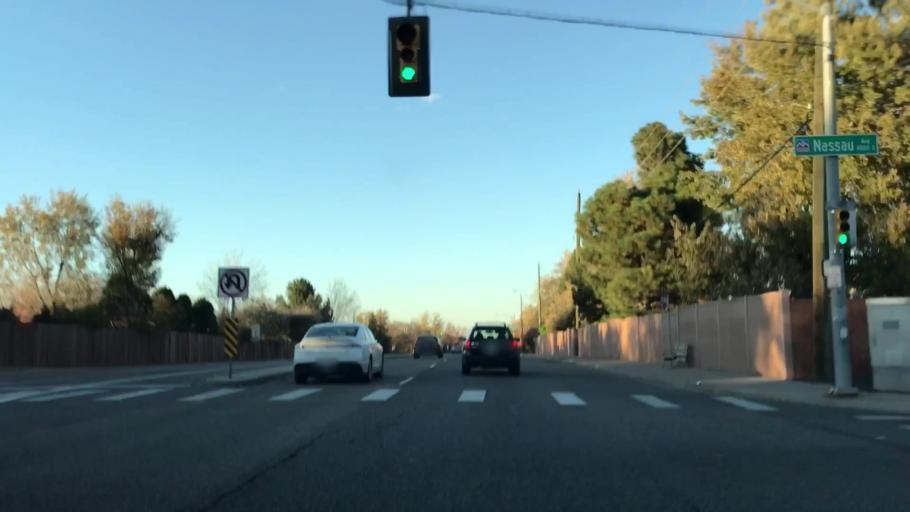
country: US
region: Colorado
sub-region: Arapahoe County
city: Castlewood
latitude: 39.6432
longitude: -104.8850
